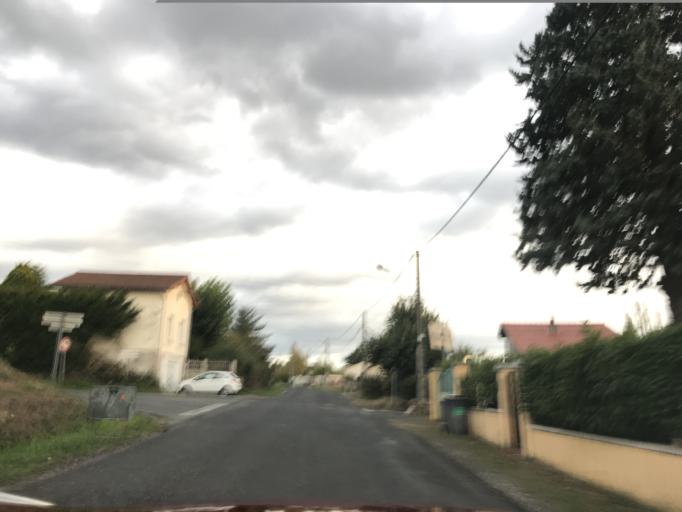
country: FR
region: Auvergne
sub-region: Departement du Puy-de-Dome
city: Thiers
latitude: 45.8399
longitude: 3.5451
